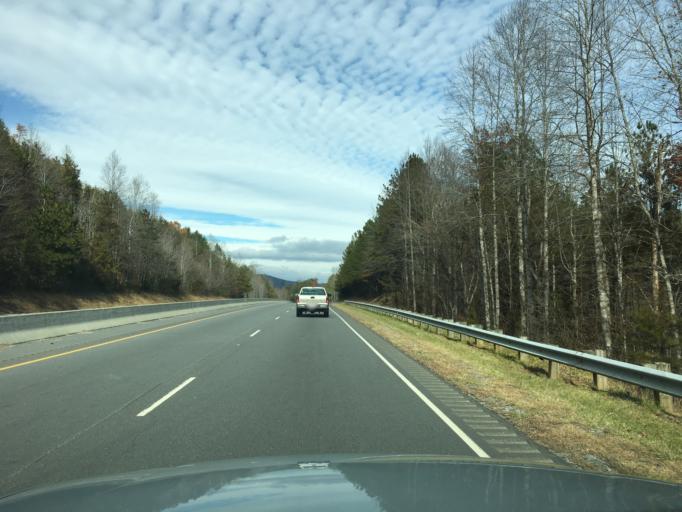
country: US
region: North Carolina
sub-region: McDowell County
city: Marion
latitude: 35.6896
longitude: -82.0304
